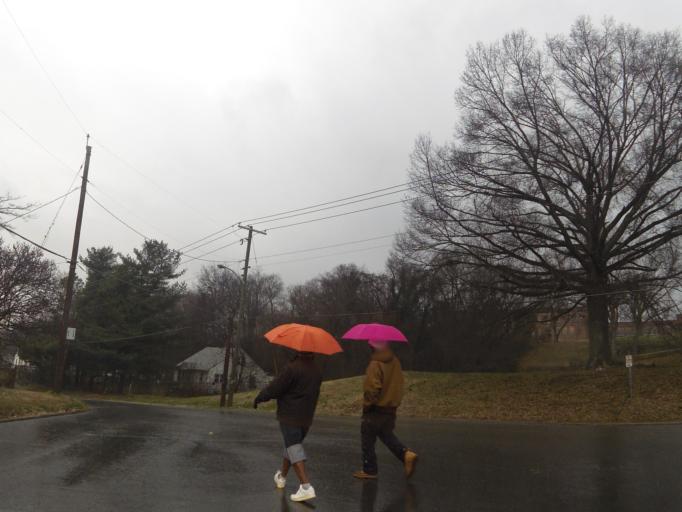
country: US
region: Tennessee
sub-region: Knox County
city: Knoxville
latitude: 35.9743
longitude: -83.9523
